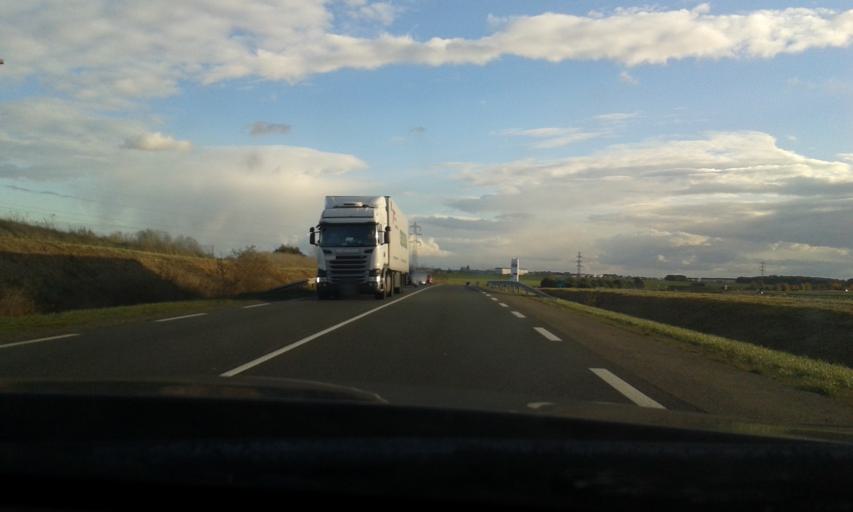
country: FR
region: Centre
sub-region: Departement d'Eure-et-Loir
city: Leves
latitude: 48.4728
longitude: 1.4630
